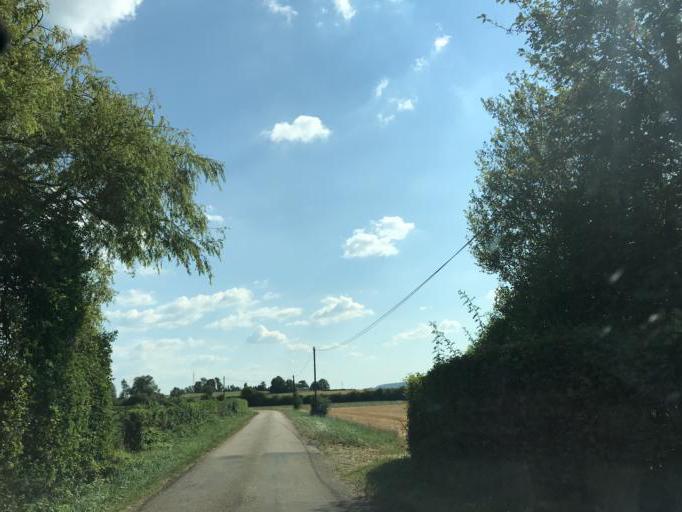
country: FR
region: Franche-Comte
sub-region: Departement du Jura
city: Clairvaux-les-Lacs
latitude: 46.5860
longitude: 5.7281
